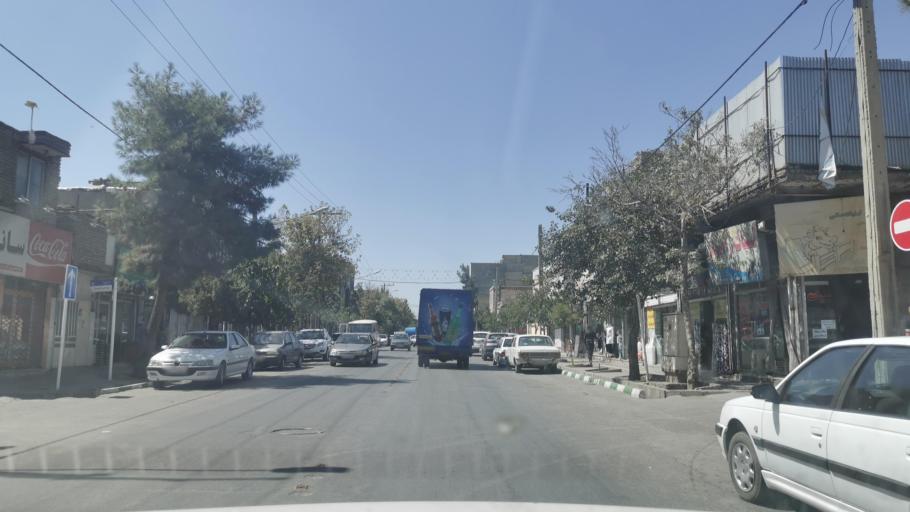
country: IR
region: Razavi Khorasan
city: Mashhad
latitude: 36.3590
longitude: 59.5494
